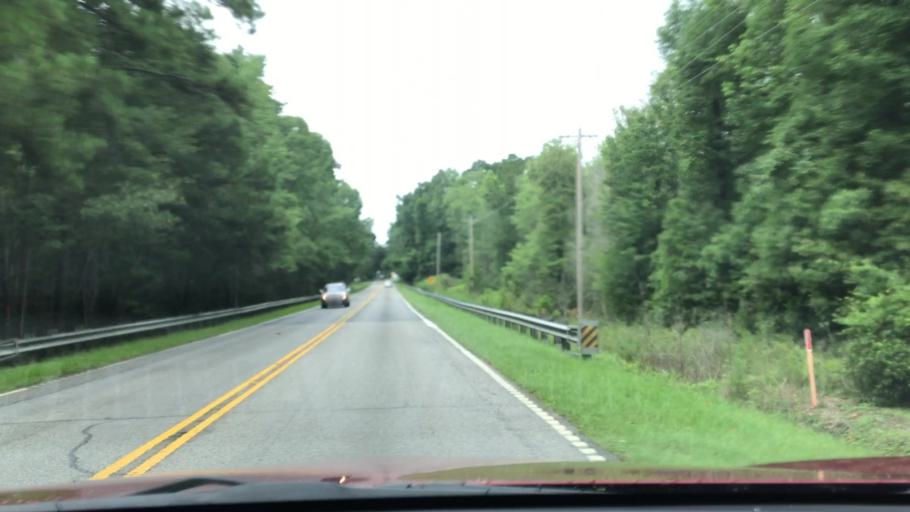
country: US
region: South Carolina
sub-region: Georgetown County
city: Murrells Inlet
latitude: 33.5595
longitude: -79.2149
